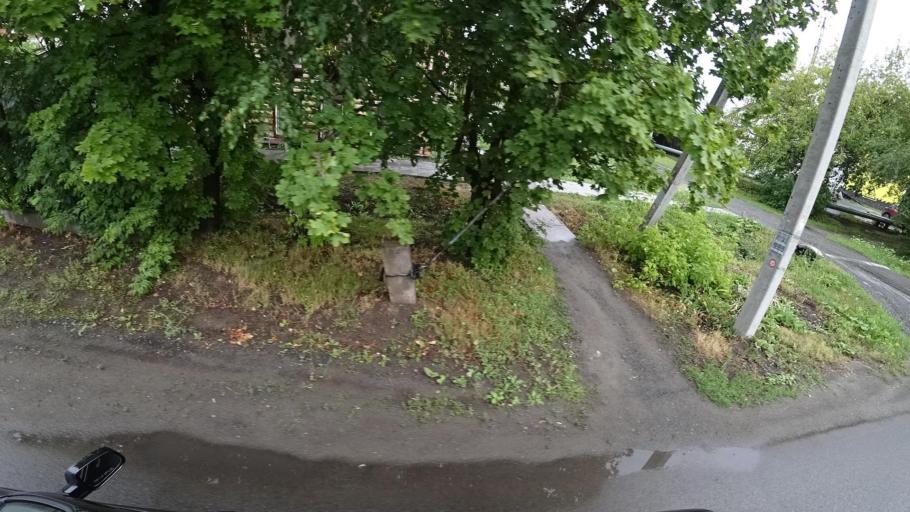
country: RU
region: Sverdlovsk
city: Kamyshlov
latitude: 56.8441
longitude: 62.7200
